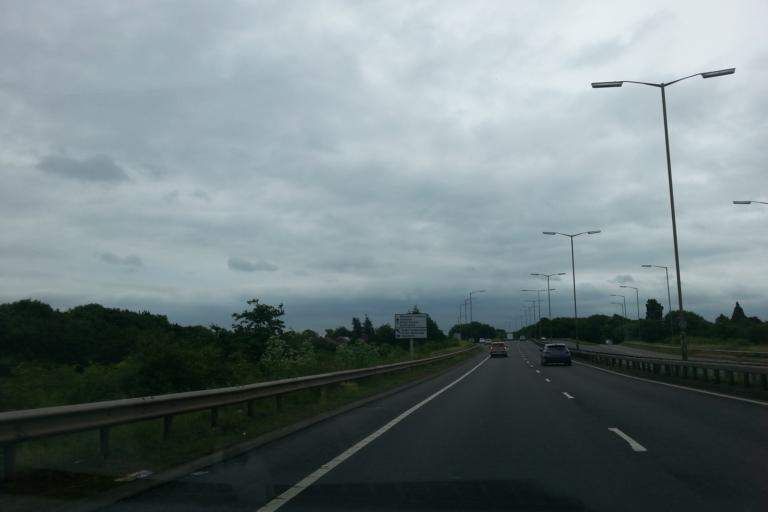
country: GB
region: England
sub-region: Peterborough
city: Peterborough
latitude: 52.5600
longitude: -0.2791
